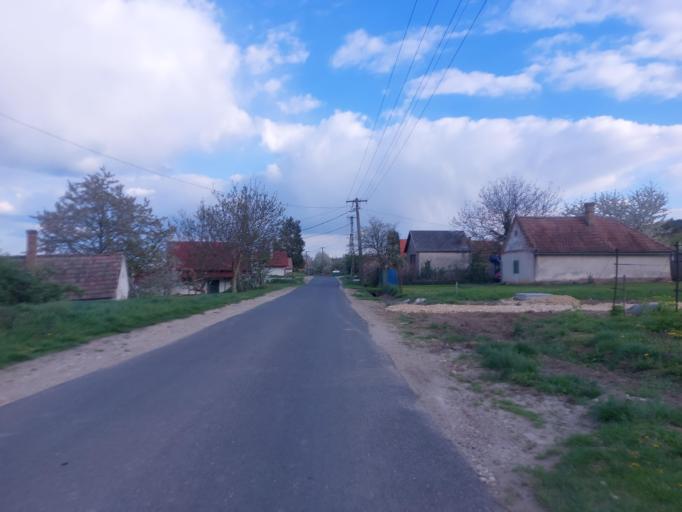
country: HU
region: Veszprem
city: Devecser
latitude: 47.1545
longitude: 17.3796
